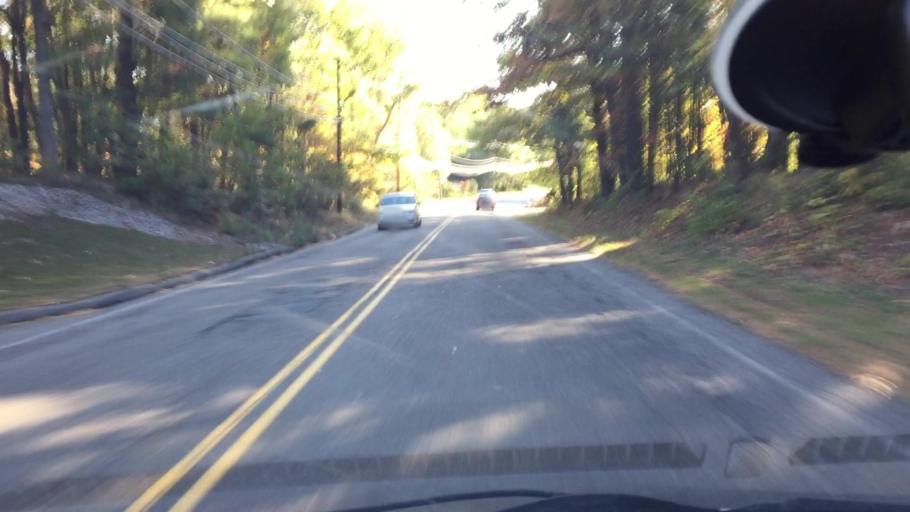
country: US
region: Massachusetts
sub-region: Norfolk County
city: Westwood
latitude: 42.2027
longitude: -71.2532
